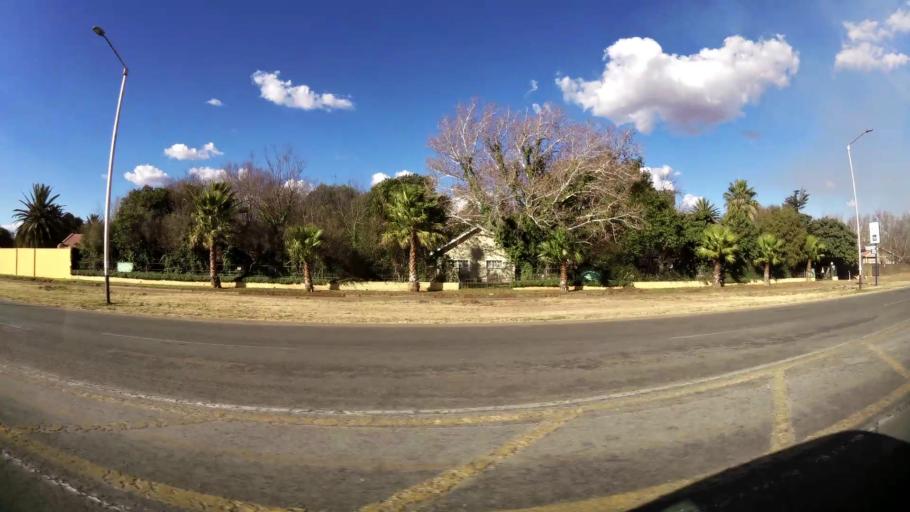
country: ZA
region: North-West
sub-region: Dr Kenneth Kaunda District Municipality
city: Klerksdorp
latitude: -26.8493
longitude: 26.6636
